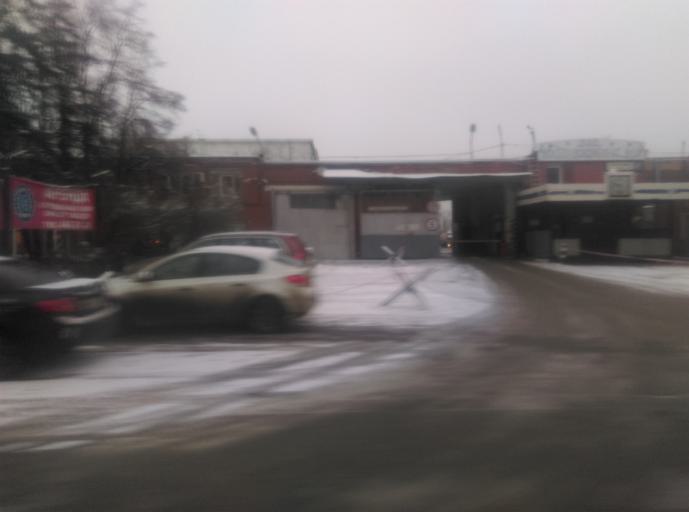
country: RU
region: Moscow
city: Mikhalkovo
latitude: 55.6956
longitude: 37.4245
